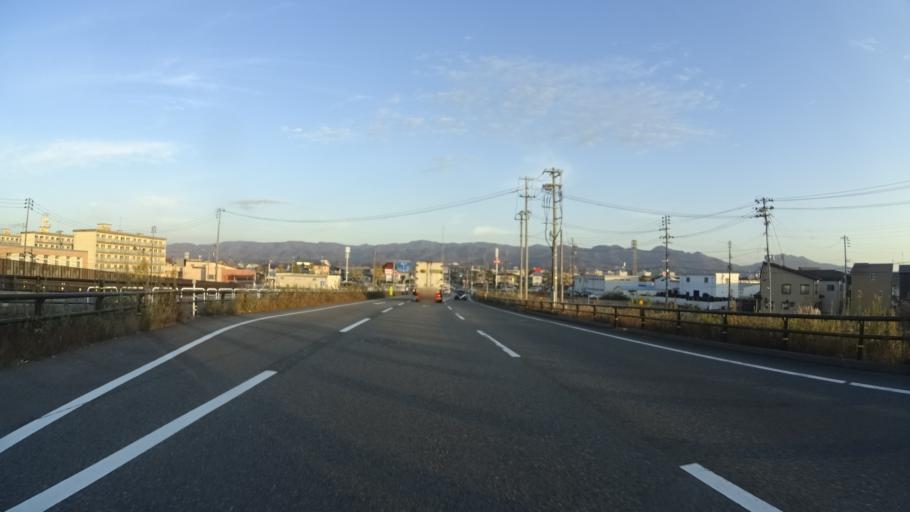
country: JP
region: Niigata
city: Nagaoka
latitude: 37.4278
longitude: 138.8337
